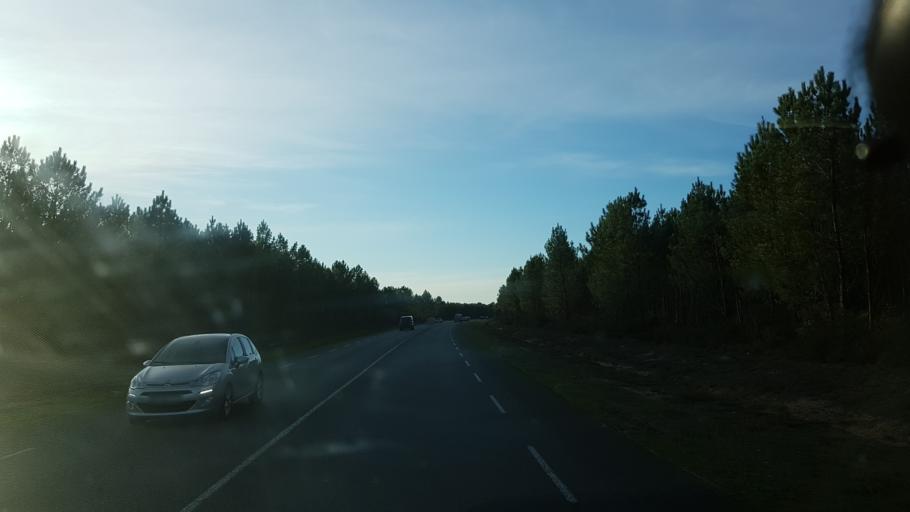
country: FR
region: Aquitaine
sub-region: Departement de la Gironde
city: Martignas-sur-Jalle
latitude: 44.8303
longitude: -0.7893
